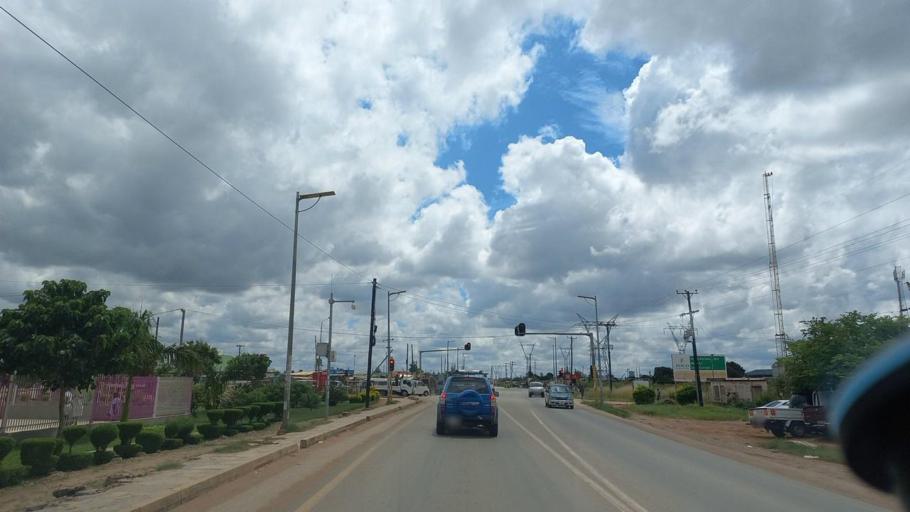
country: ZM
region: Lusaka
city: Lusaka
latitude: -15.4510
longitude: 28.3163
